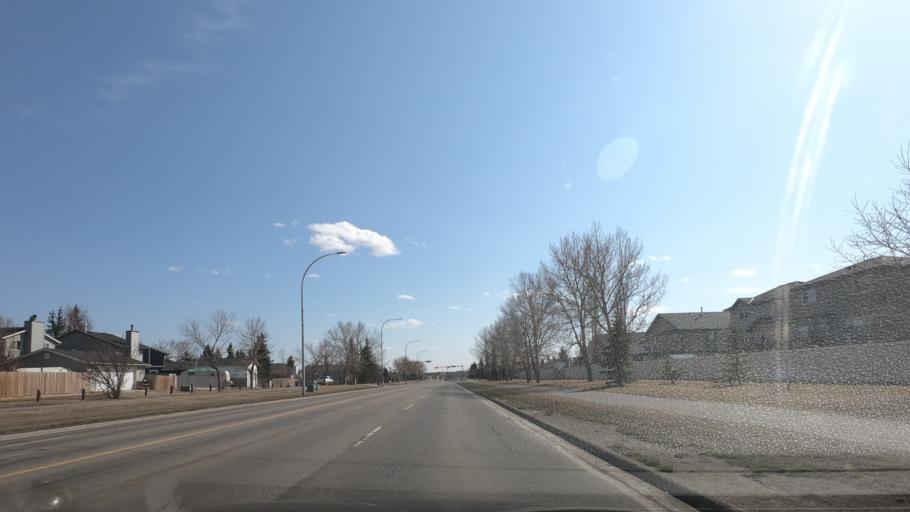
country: CA
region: Alberta
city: Airdrie
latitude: 51.2748
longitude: -113.9899
